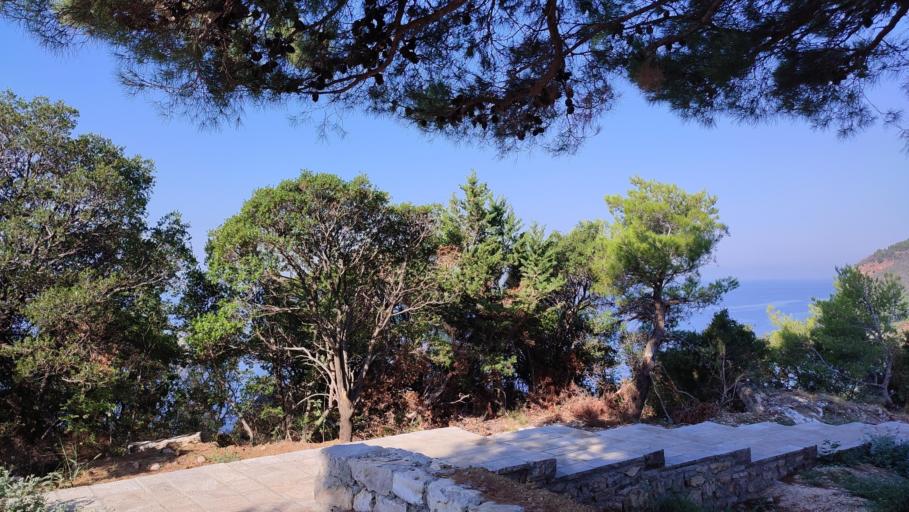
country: ME
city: Petrovac na Moru
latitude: 42.2020
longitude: 18.9453
